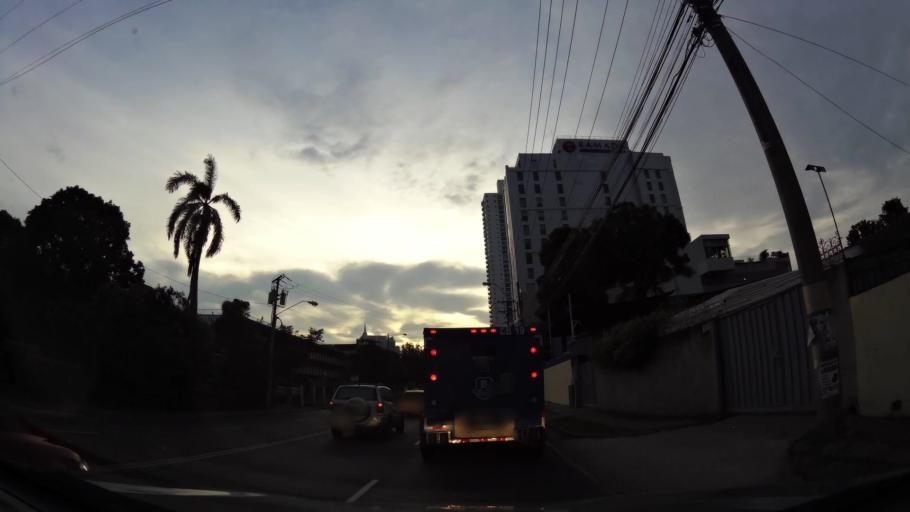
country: PA
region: Panama
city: Panama
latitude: 8.9875
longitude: -79.5063
